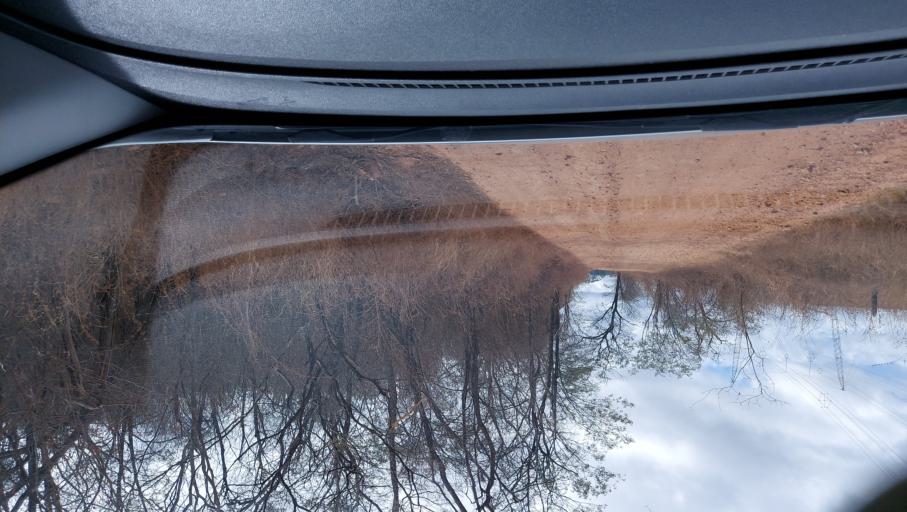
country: BR
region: Bahia
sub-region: Oliveira Dos Brejinhos
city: Beira Rio
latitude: -12.0871
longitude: -42.5434
